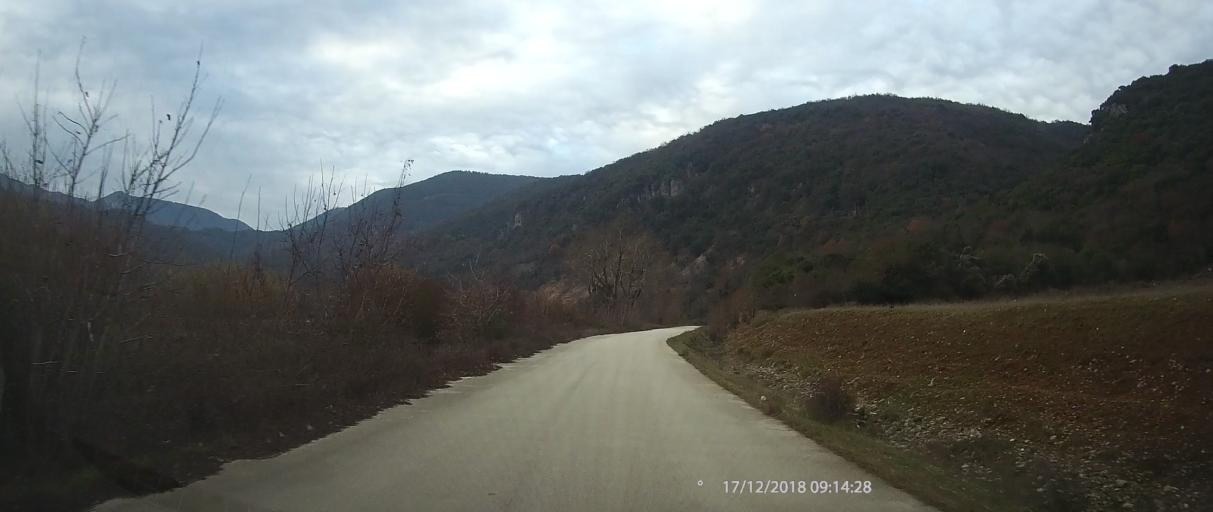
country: GR
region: Epirus
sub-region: Nomos Ioanninon
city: Kalpaki
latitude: 39.9733
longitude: 20.6559
